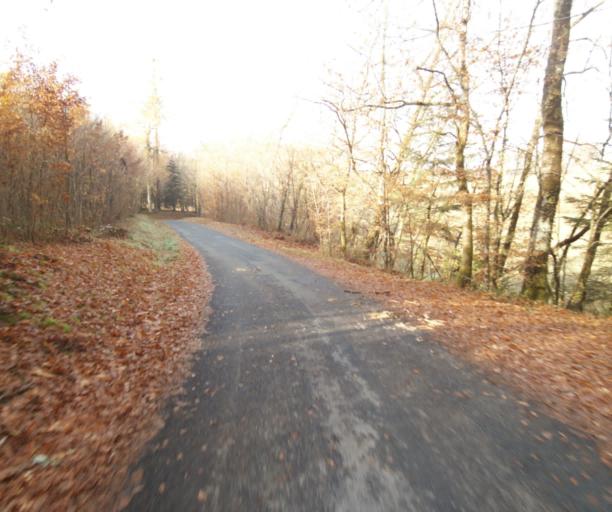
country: FR
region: Limousin
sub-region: Departement de la Correze
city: Chameyrat
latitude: 45.2279
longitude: 1.7356
